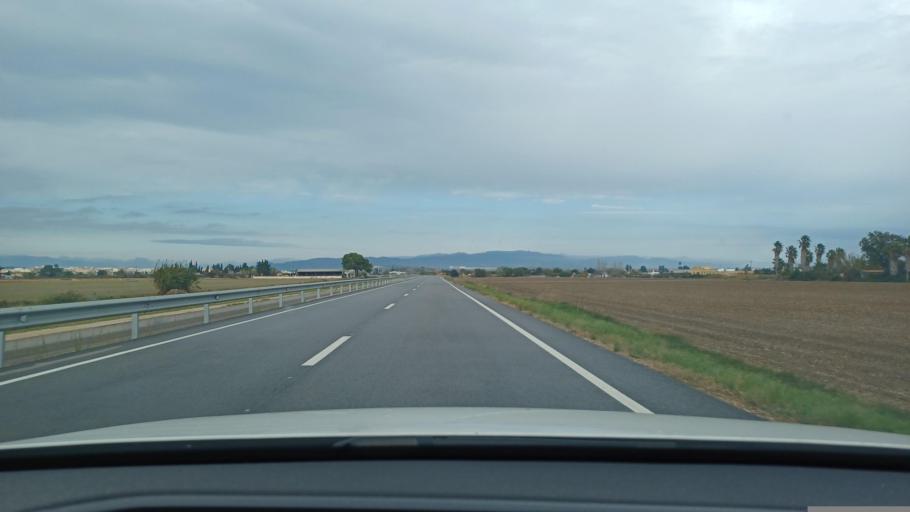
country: ES
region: Catalonia
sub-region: Provincia de Tarragona
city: Amposta
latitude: 40.6879
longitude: 0.5904
